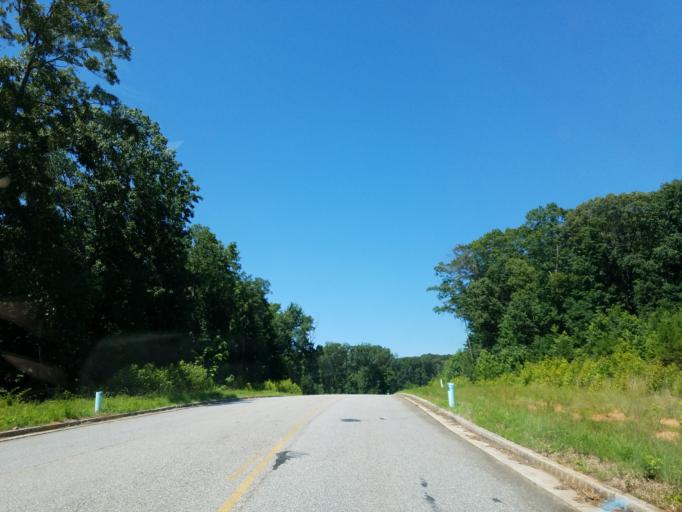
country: US
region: Georgia
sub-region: Forsyth County
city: Cumming
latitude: 34.2708
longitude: -84.0776
